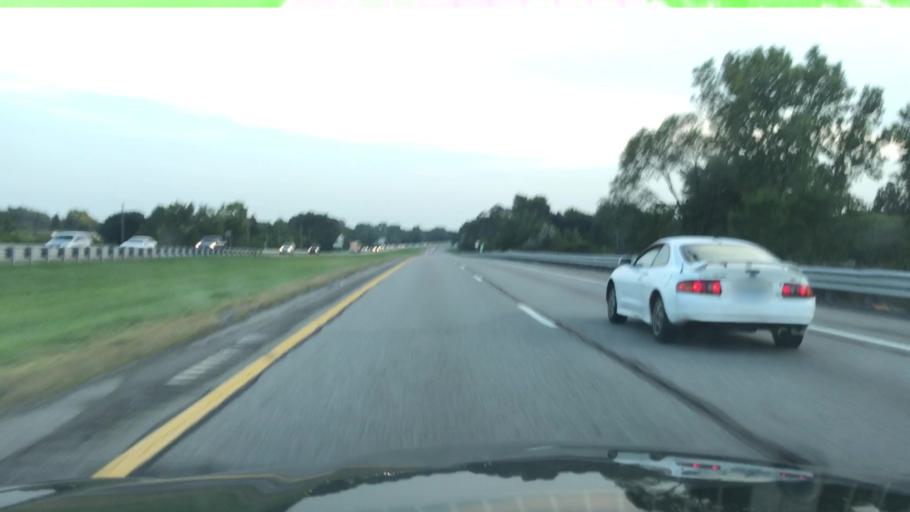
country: US
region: Michigan
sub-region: Macomb County
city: Utica
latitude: 42.6194
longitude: -83.0125
